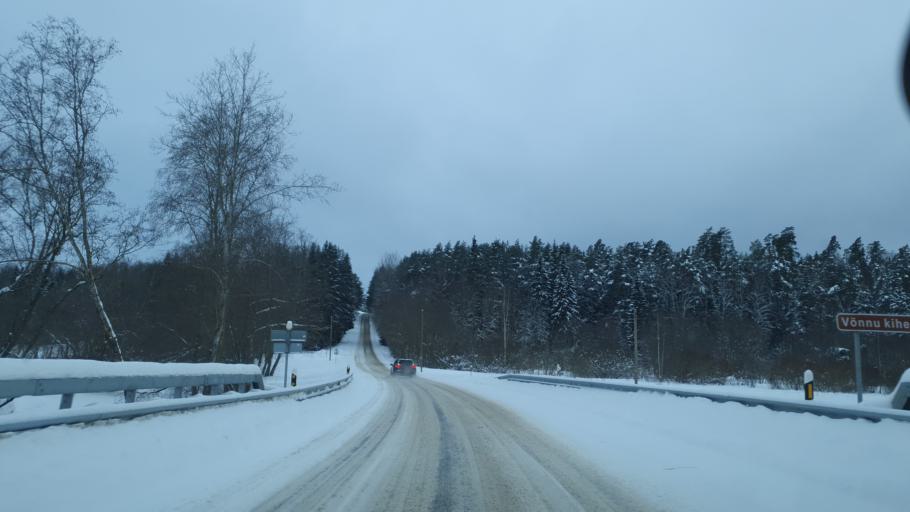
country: EE
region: Polvamaa
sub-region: Polva linn
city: Polva
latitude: 58.1156
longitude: 27.0867
